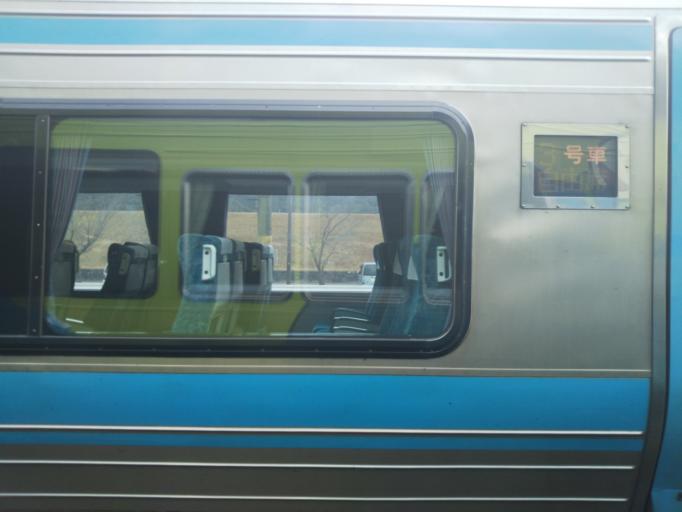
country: JP
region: Kochi
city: Nakamura
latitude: 32.9843
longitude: 132.9442
